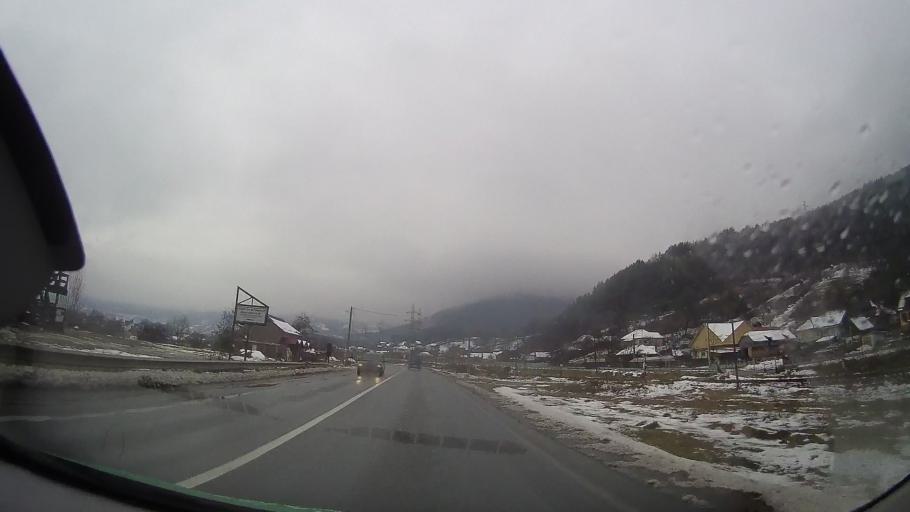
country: RO
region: Neamt
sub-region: Comuna Pangarati
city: Oantu
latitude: 46.9286
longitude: 26.1977
